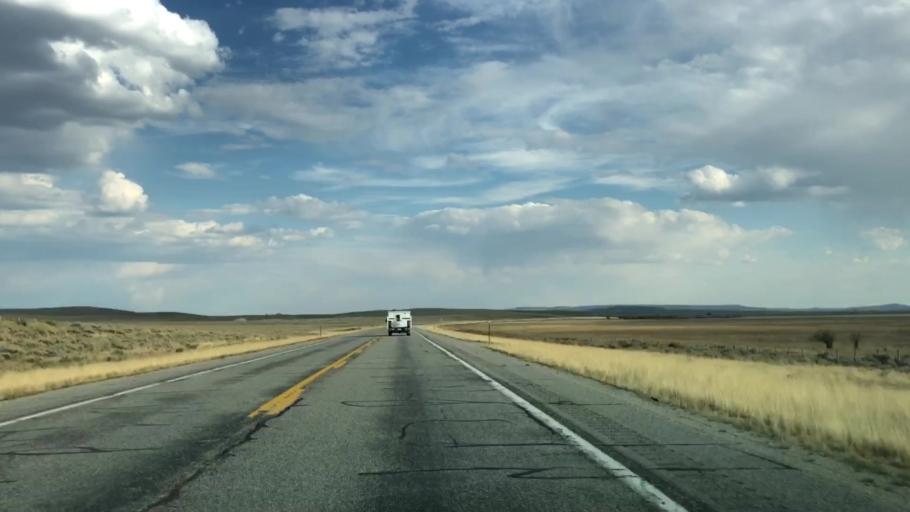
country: US
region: Wyoming
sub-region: Sublette County
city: Pinedale
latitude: 43.0368
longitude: -110.1345
